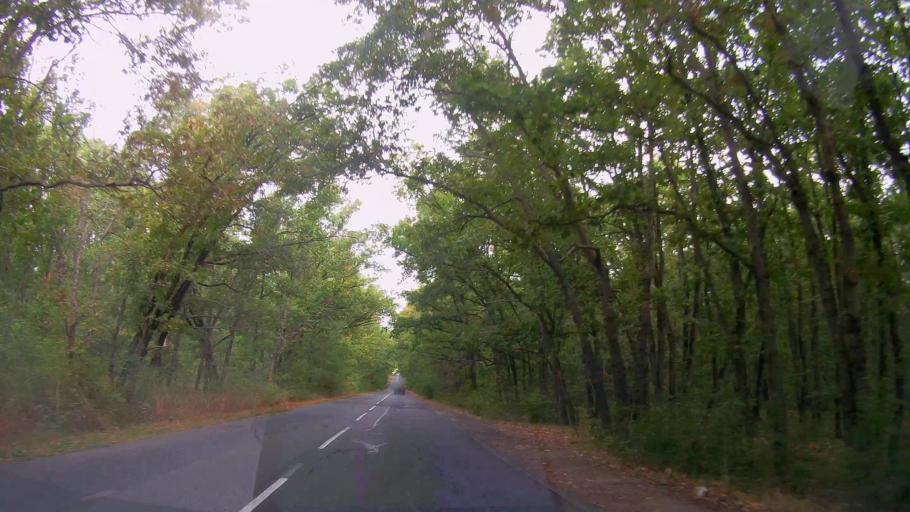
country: BG
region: Burgas
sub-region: Obshtina Primorsko
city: Primorsko
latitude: 42.2792
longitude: 27.7391
